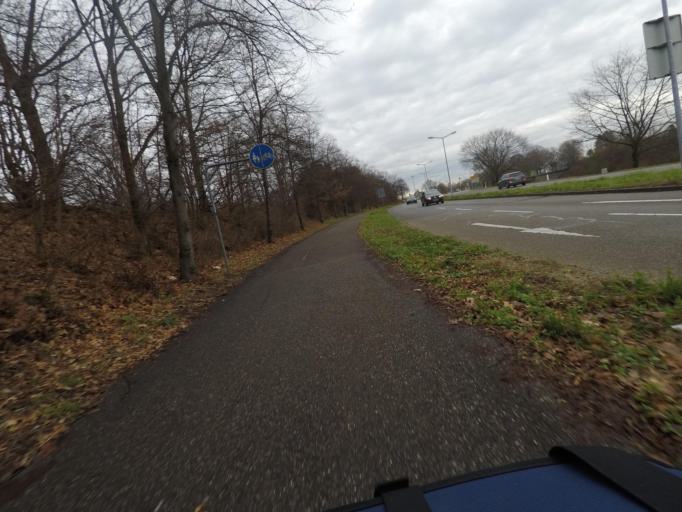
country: DE
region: Baden-Wuerttemberg
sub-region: Karlsruhe Region
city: Rheinstetten
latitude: 48.9939
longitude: 8.3410
